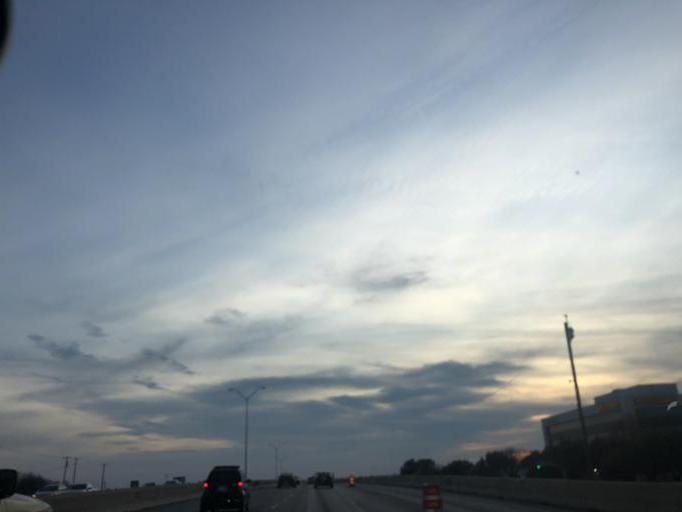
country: US
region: Texas
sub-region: Dallas County
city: Duncanville
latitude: 32.6777
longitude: -96.8561
